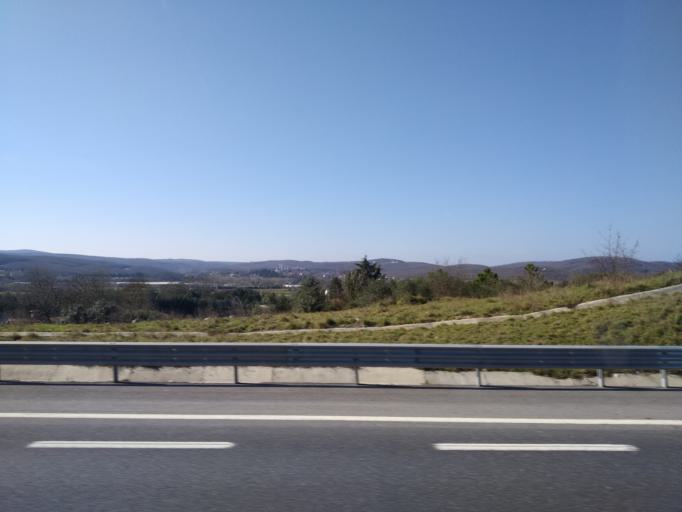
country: TR
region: Istanbul
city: Mahmut Sevket Pasa
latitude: 41.1298
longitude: 29.2861
